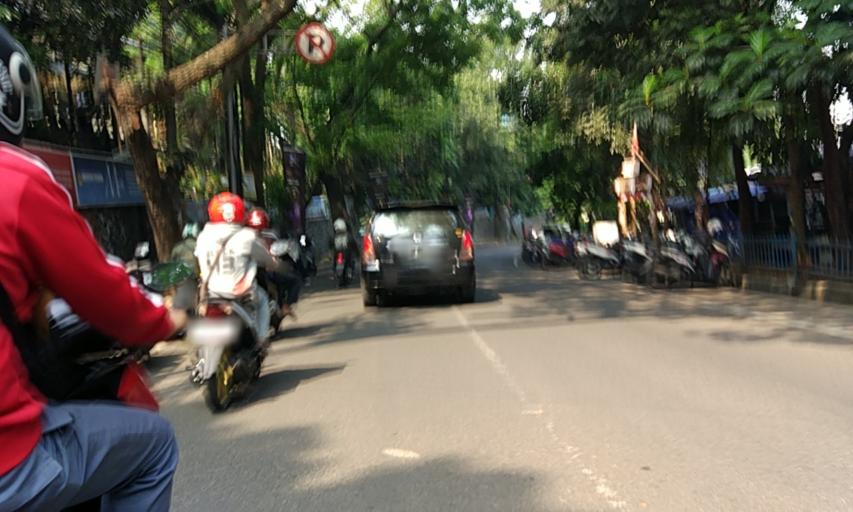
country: ID
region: West Java
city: Bandung
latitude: -6.9046
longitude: 107.6081
